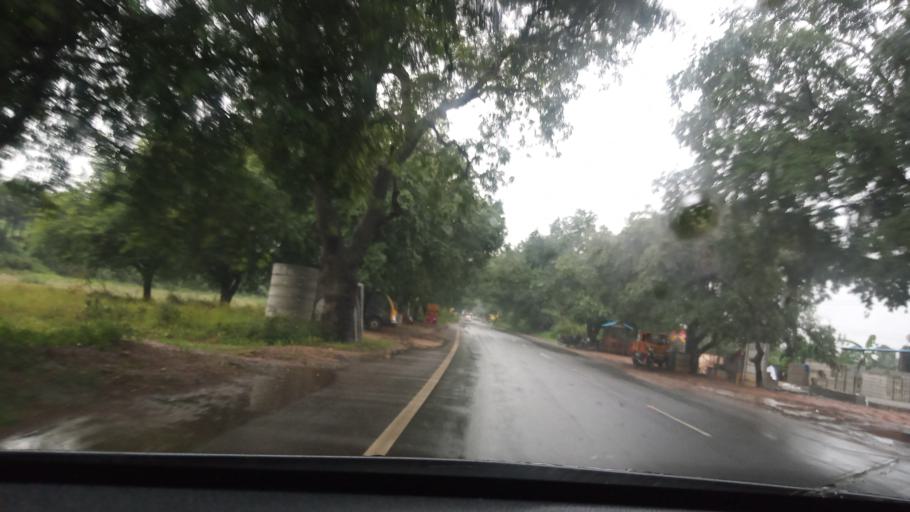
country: IN
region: Tamil Nadu
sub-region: Vellore
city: Kalavai
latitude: 12.8052
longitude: 79.4197
